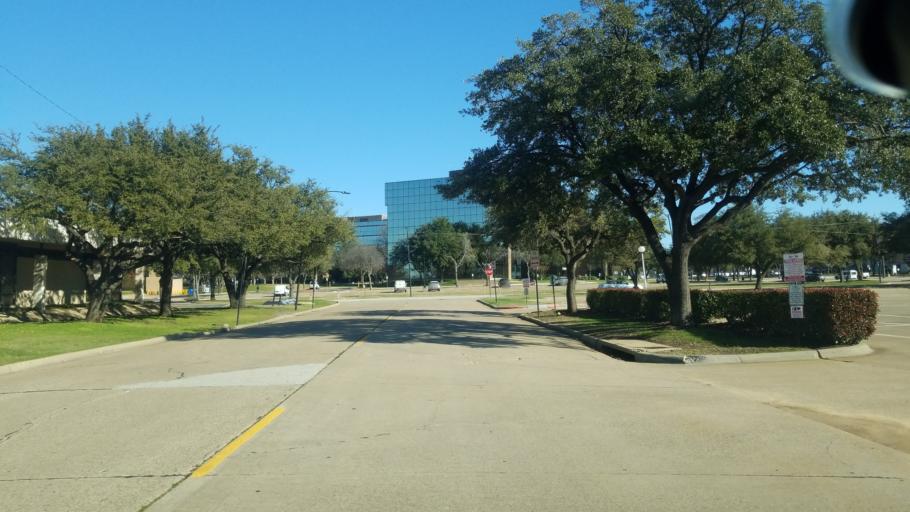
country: US
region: Texas
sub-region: Tarrant County
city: Arlington
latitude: 32.7494
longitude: -97.0697
